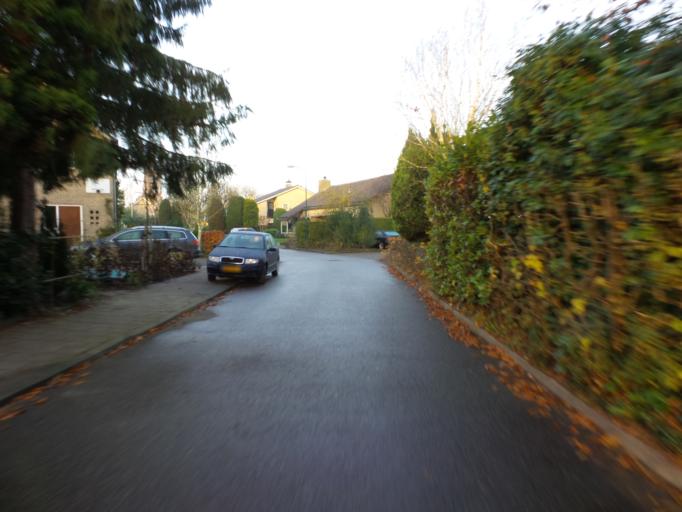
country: NL
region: Utrecht
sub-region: Gemeente Leusden
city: Leusden
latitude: 52.1222
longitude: 5.4080
